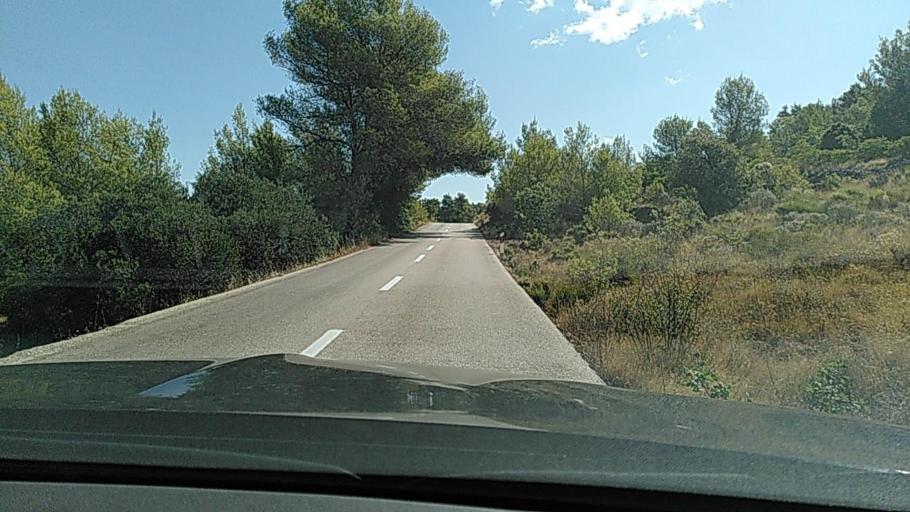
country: HR
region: Splitsko-Dalmatinska
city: Jelsa
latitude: 43.1433
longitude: 16.8196
